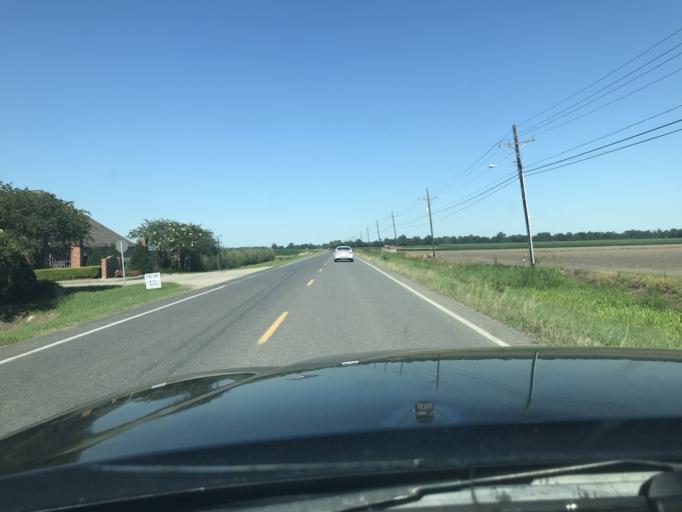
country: US
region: Louisiana
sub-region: West Baton Rouge Parish
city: Brusly
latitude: 30.4683
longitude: -91.3037
